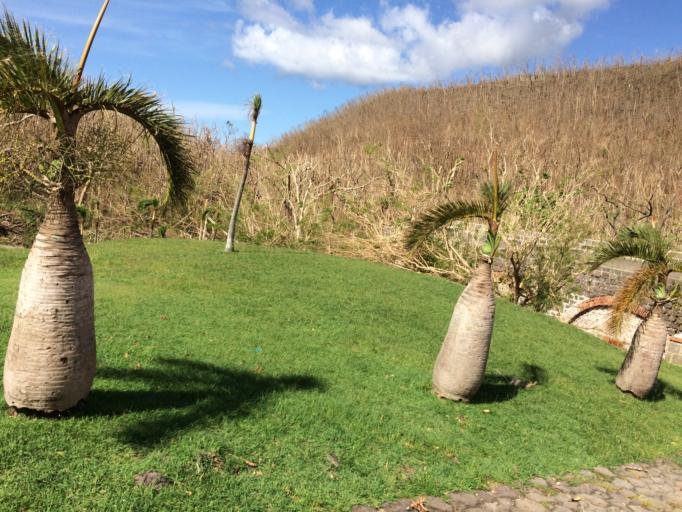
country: DM
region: Saint John
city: Portsmouth
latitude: 15.5835
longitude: -61.4736
